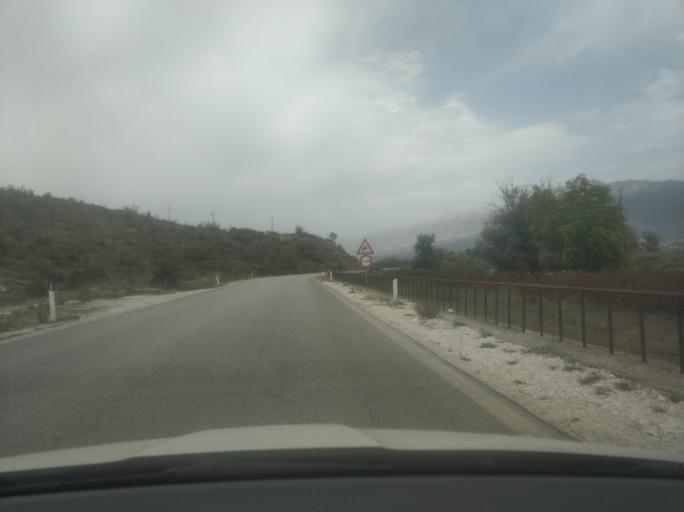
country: AL
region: Gjirokaster
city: Gjirokaster
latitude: 40.1066
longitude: 20.1228
